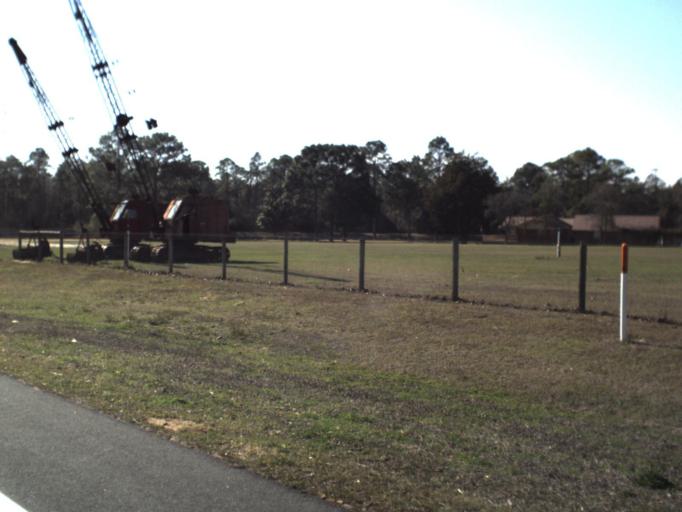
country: US
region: Florida
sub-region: Bay County
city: Youngstown
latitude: 30.4281
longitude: -85.2914
